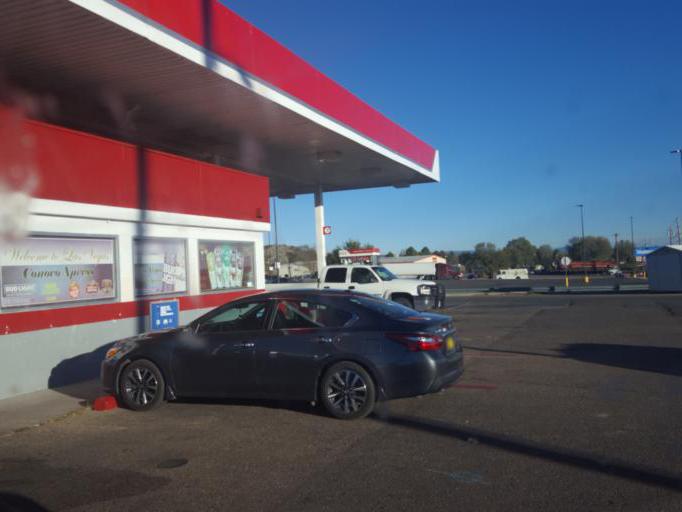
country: US
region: New Mexico
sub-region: San Miguel County
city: Las Vegas
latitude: 35.6193
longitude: -105.2258
